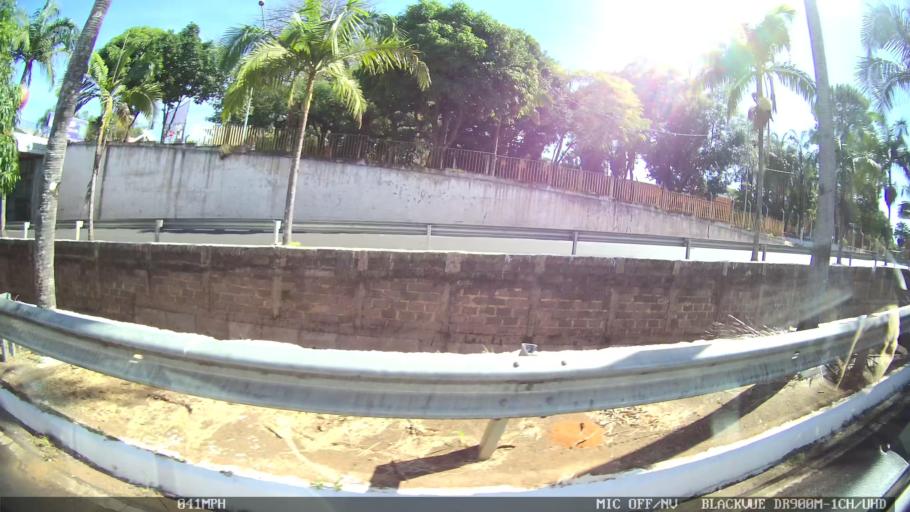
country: BR
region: Sao Paulo
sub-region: Franca
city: Franca
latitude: -20.5326
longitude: -47.4049
